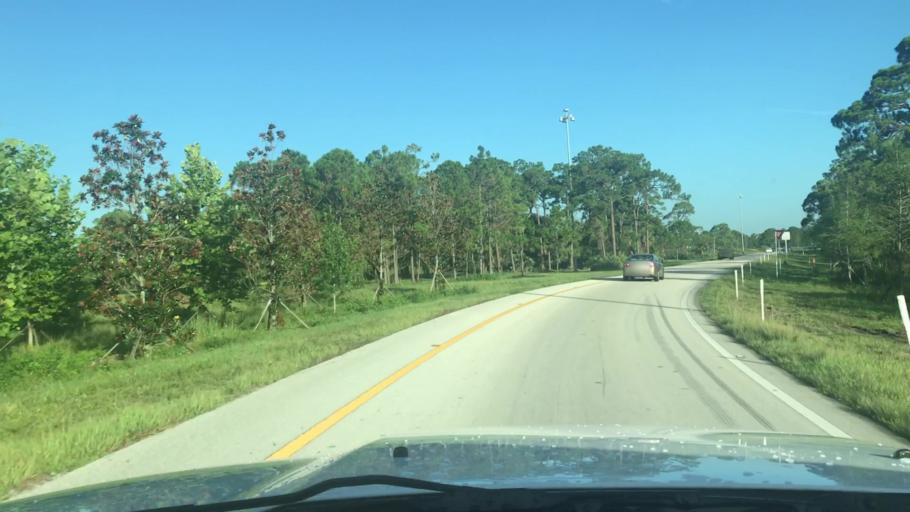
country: US
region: Florida
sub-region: Martin County
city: Palm City
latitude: 27.1620
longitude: -80.3870
